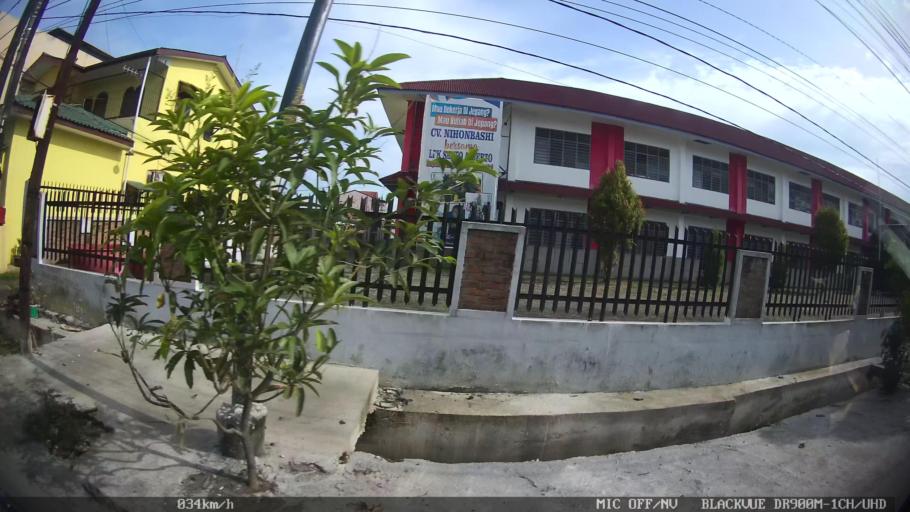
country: ID
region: North Sumatra
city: Medan
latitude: 3.6104
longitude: 98.6376
